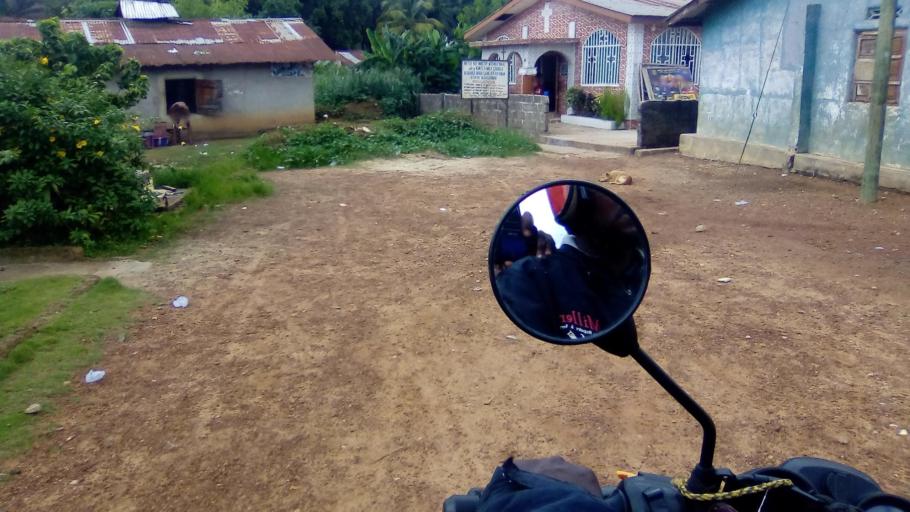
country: SL
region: Southern Province
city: Bo
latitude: 7.9565
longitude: -11.7451
